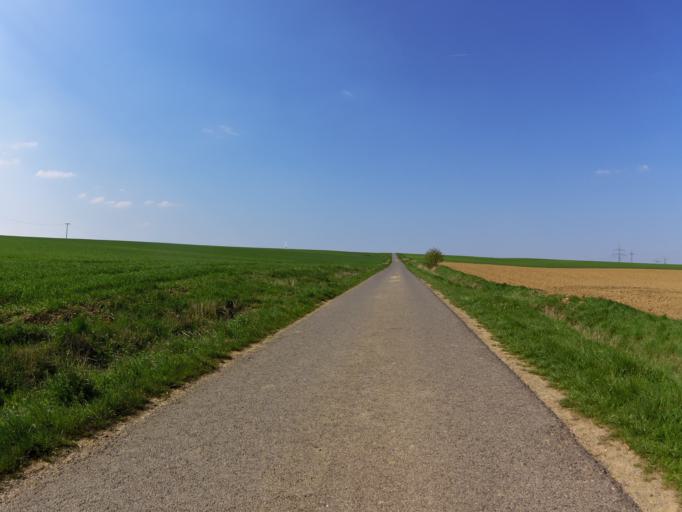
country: DE
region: Bavaria
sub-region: Regierungsbezirk Unterfranken
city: Theilheim
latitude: 49.7585
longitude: 10.0478
